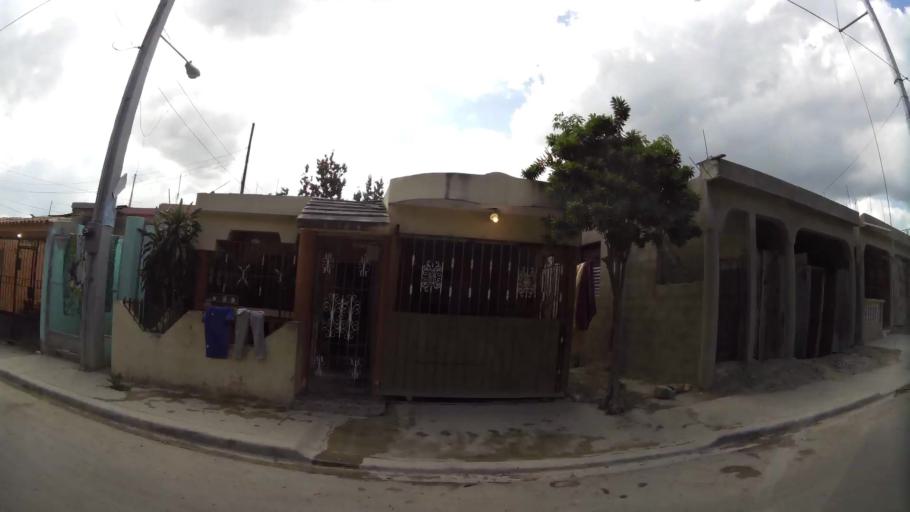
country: DO
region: Nacional
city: Ensanche Luperon
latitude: 18.5363
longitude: -69.8848
